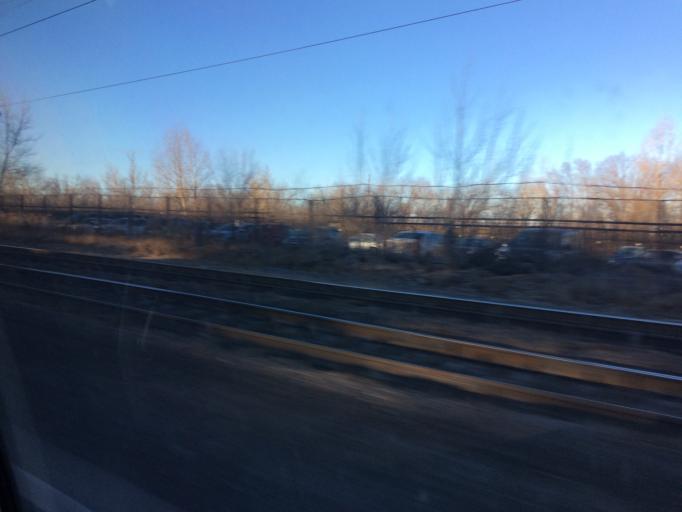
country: RU
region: Chelyabinsk
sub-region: Gorod Magnitogorsk
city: Magnitogorsk
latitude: 53.4044
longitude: 59.0278
